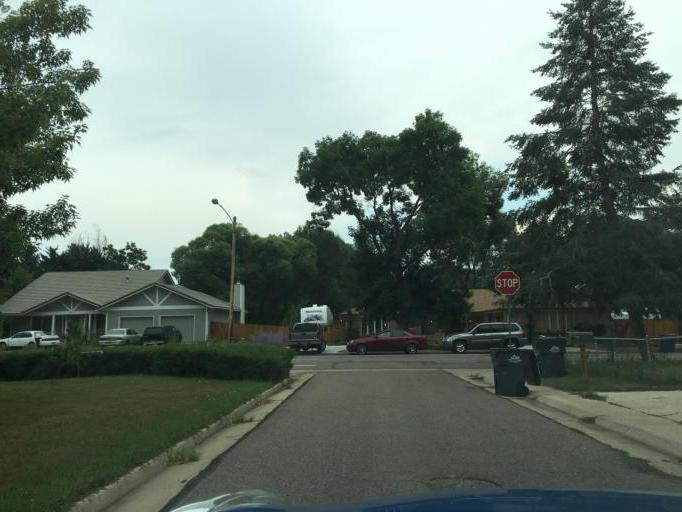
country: US
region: Colorado
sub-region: Jefferson County
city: Wheat Ridge
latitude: 39.7521
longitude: -105.0912
